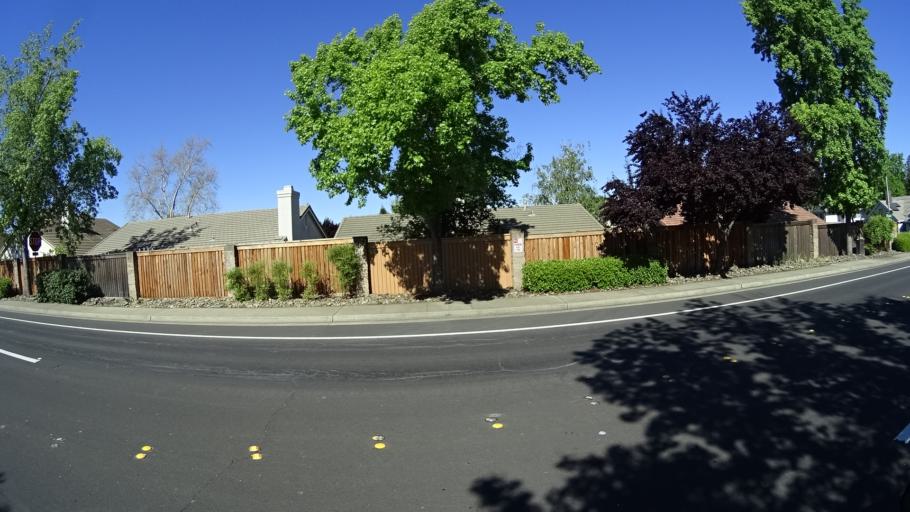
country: US
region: California
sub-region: Placer County
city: Rocklin
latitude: 38.7868
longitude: -121.2636
